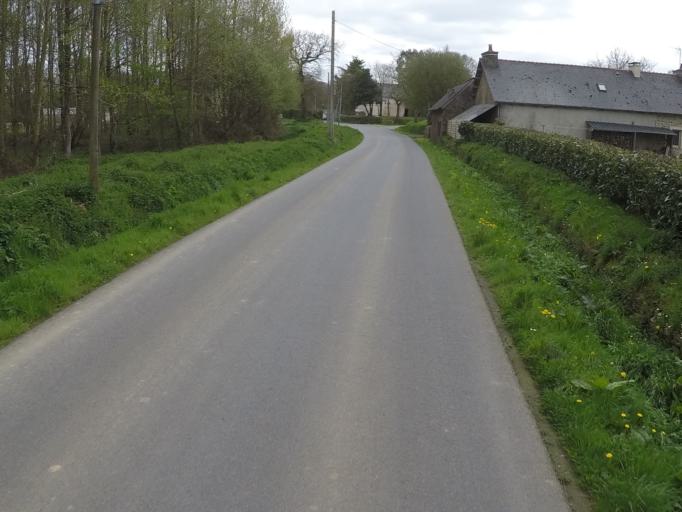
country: FR
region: Brittany
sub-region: Departement des Cotes-d'Armor
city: Plouha
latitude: 48.6609
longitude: -2.9172
